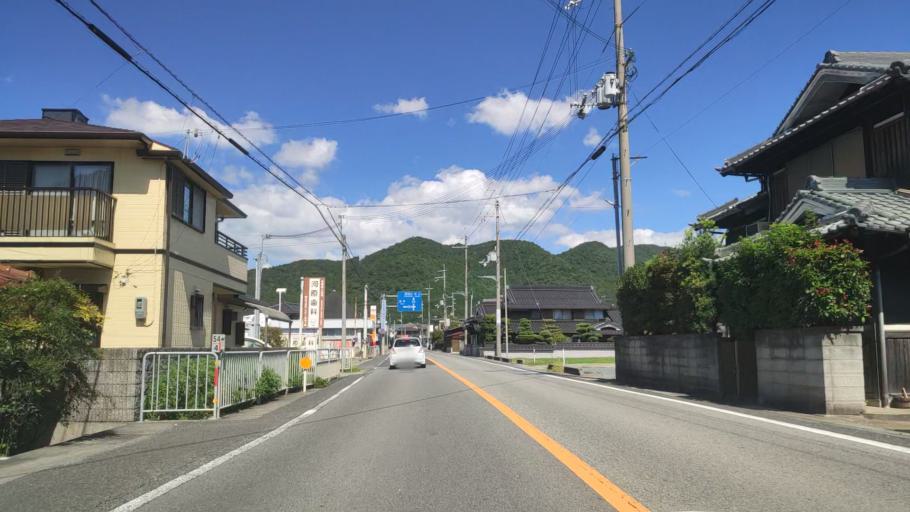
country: JP
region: Hyogo
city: Nishiwaki
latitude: 35.0766
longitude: 135.0074
